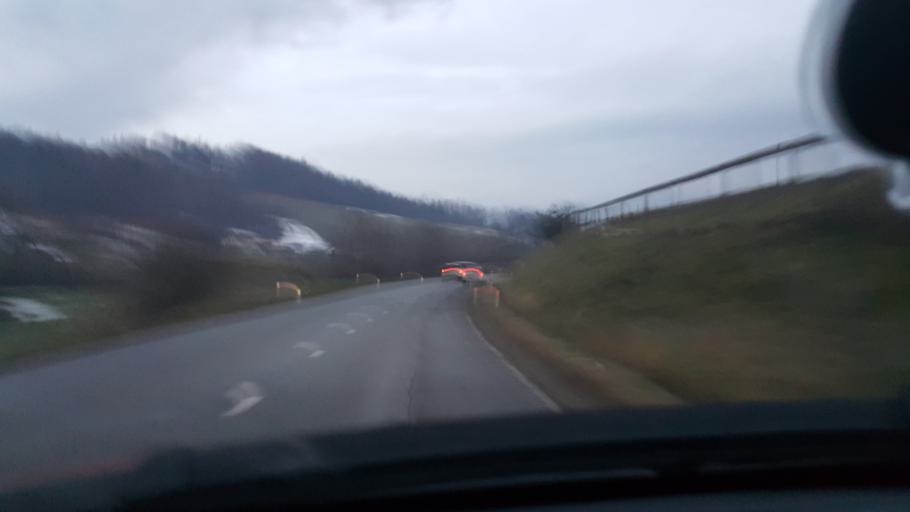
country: SI
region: Kungota
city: Zgornja Kungota
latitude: 46.6203
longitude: 15.6348
